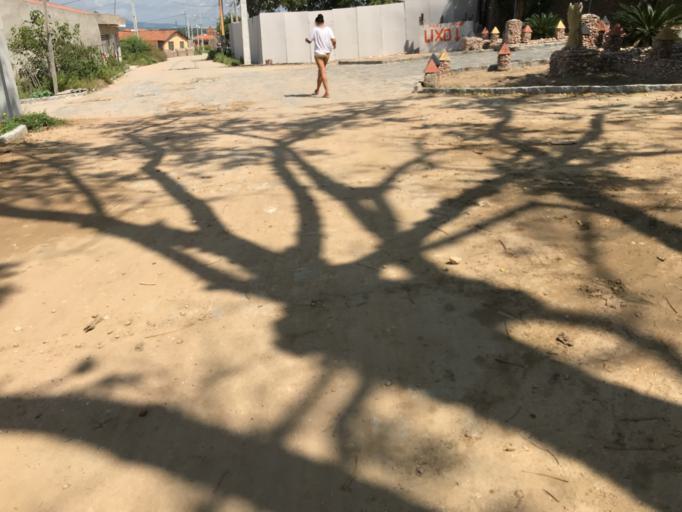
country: BR
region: Pernambuco
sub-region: Bezerros
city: Bezerros
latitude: -8.2275
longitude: -35.7563
